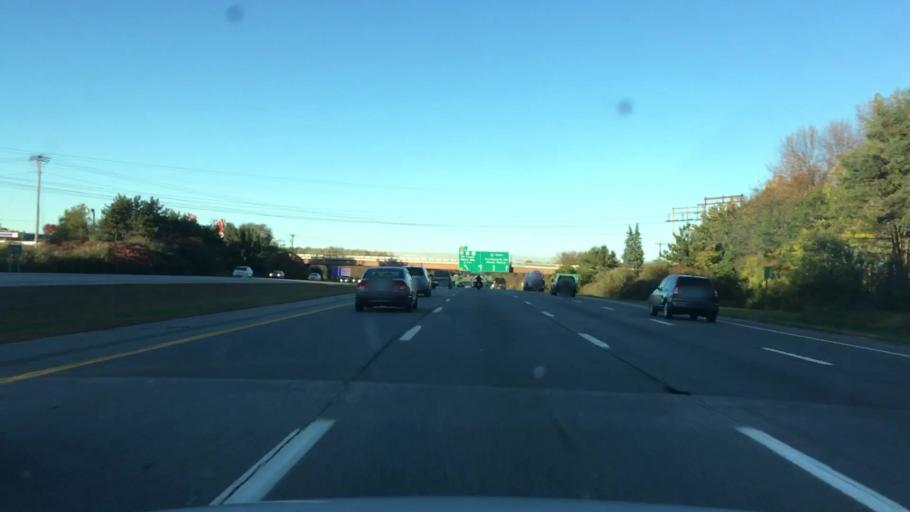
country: US
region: New Hampshire
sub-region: Rockingham County
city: Greenland
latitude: 43.0403
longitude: -70.8178
